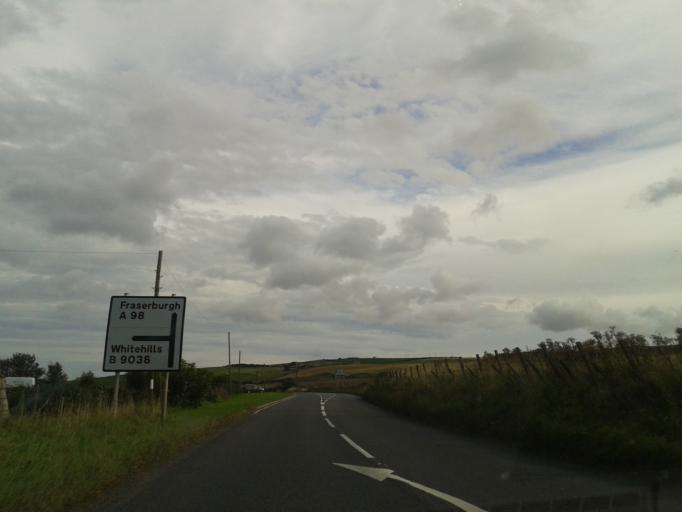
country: GB
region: Scotland
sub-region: Aberdeenshire
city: Whitehills
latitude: 57.6647
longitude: -2.5662
